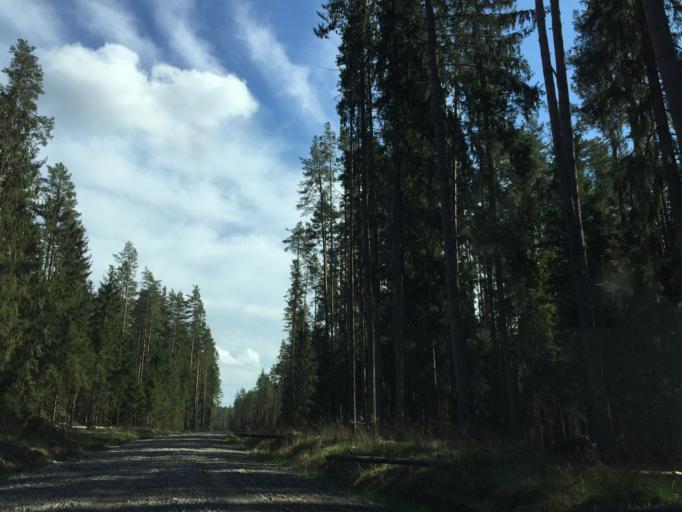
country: LV
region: Strenci
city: Strenci
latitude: 57.5902
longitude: 25.6996
